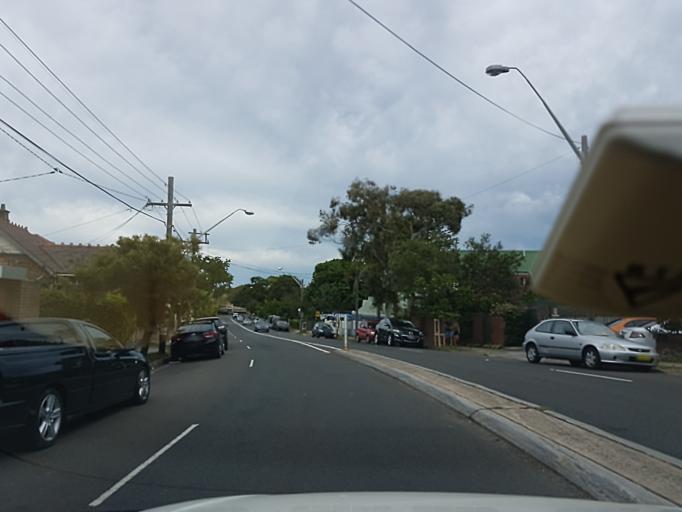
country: AU
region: New South Wales
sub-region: Warringah
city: Freshwater
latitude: -33.7871
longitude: 151.2840
